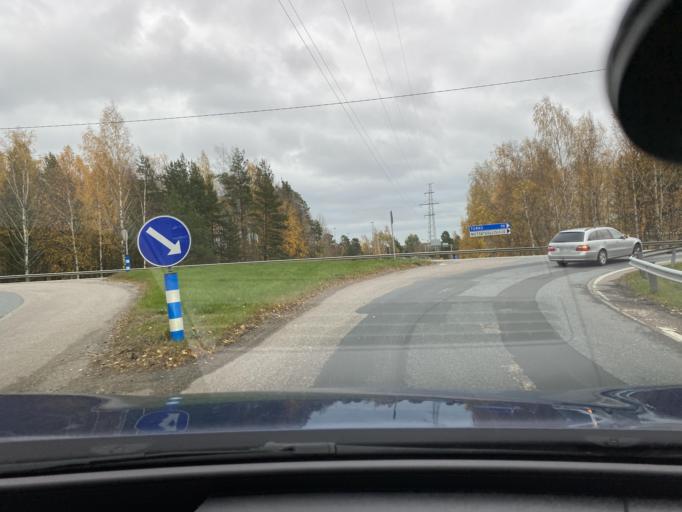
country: FI
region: Satakunta
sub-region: Rauma
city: Rauma
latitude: 61.1336
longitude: 21.5353
